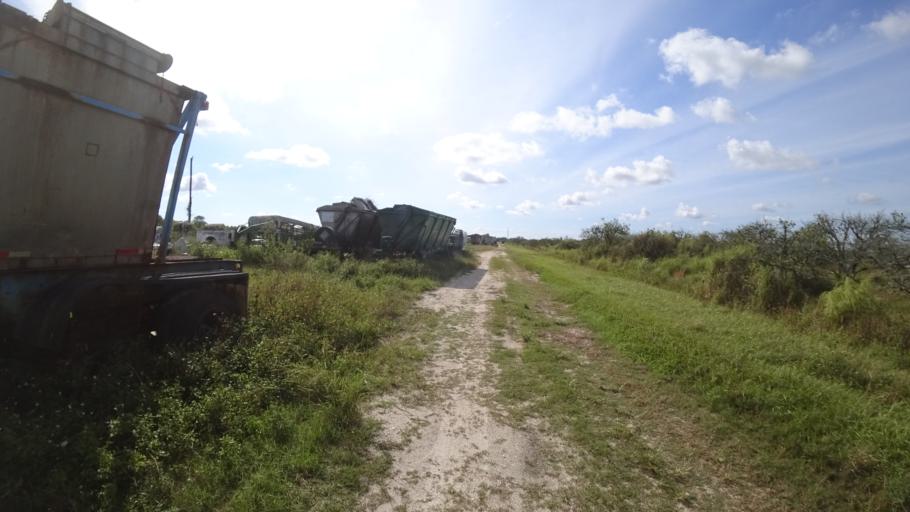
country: US
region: Florida
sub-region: Hillsborough County
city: Wimauma
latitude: 27.6083
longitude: -82.2879
